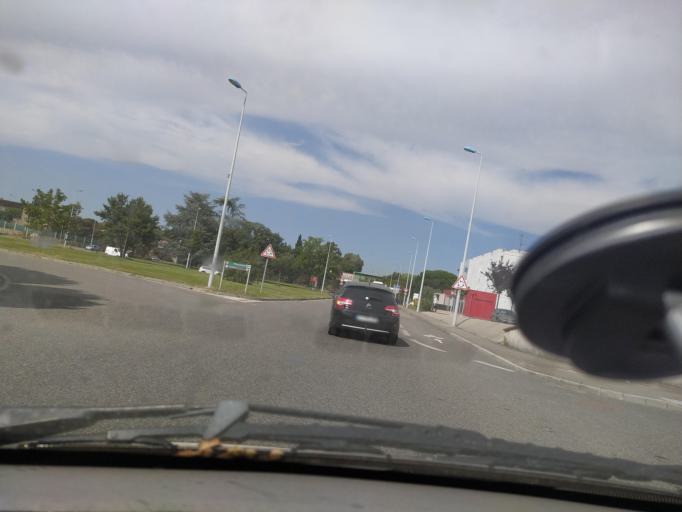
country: FR
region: Midi-Pyrenees
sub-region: Departement de la Haute-Garonne
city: Colomiers
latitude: 43.6049
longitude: 1.3355
